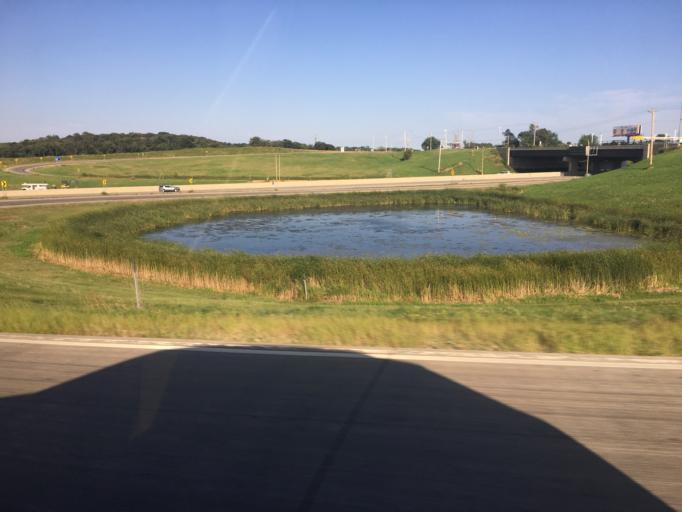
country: US
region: Minnesota
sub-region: Olmsted County
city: Oronoco
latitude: 44.0950
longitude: -92.5141
